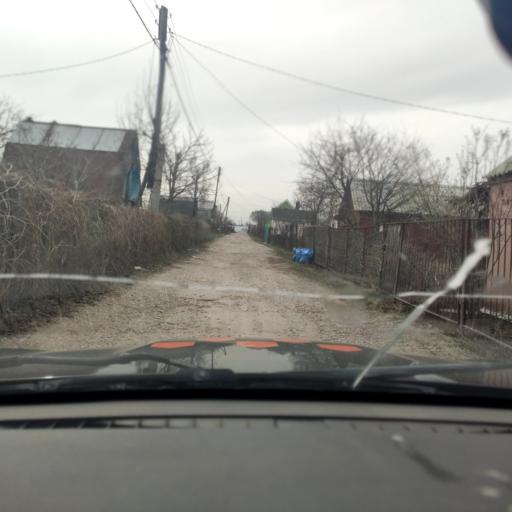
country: RU
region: Samara
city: Tol'yatti
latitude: 53.5972
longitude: 49.2458
